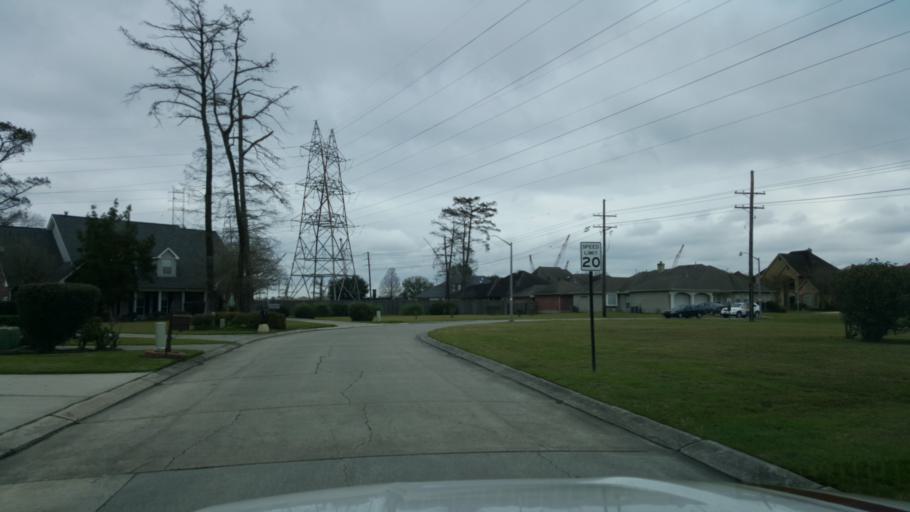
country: US
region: Louisiana
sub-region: Jefferson Parish
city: Harvey
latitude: 29.8816
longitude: -90.0801
